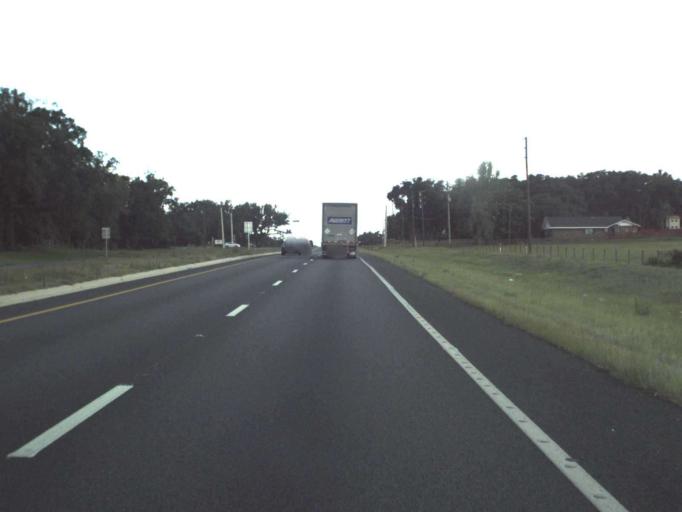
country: US
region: Florida
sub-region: Sumter County
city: Wildwood
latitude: 28.9045
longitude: -82.0372
